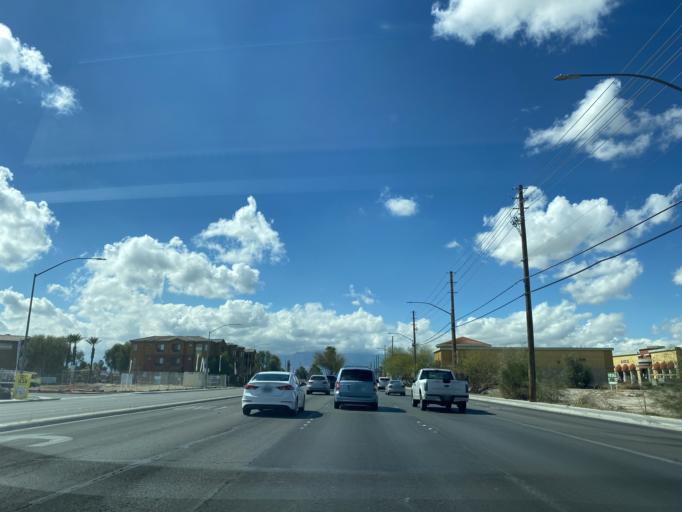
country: US
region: Nevada
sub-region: Clark County
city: Las Vegas
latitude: 36.2394
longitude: -115.1910
